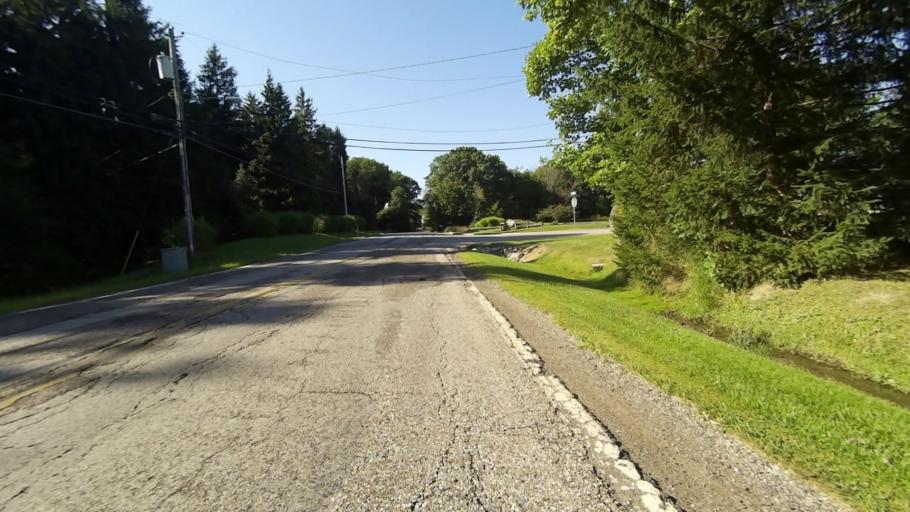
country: US
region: Ohio
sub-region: Portage County
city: Streetsboro
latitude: 41.2295
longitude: -81.3097
